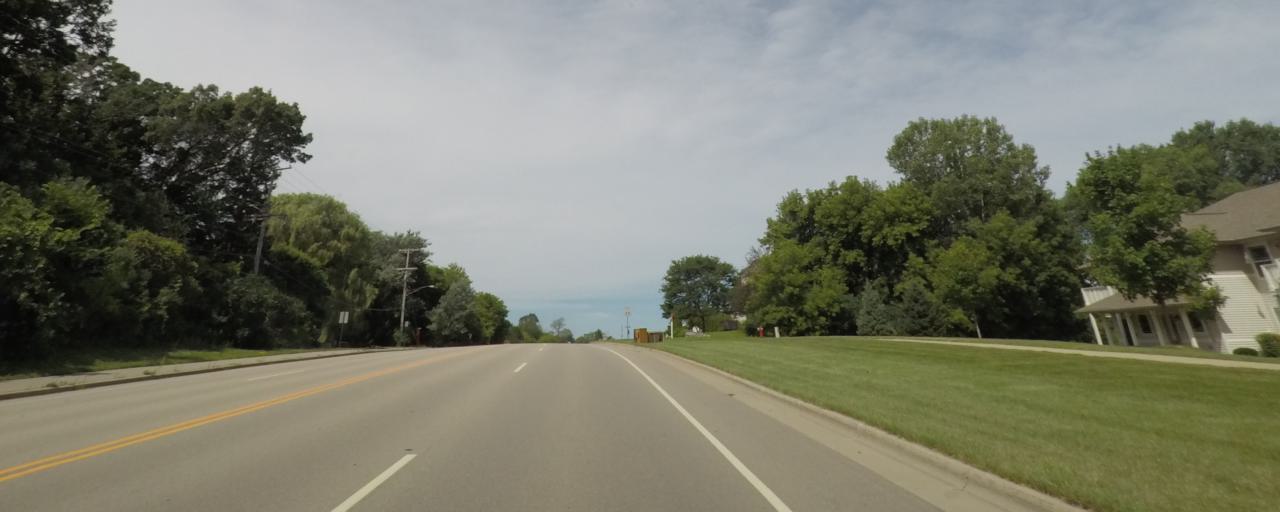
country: US
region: Wisconsin
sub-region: Dane County
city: McFarland
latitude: 43.0260
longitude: -89.2958
